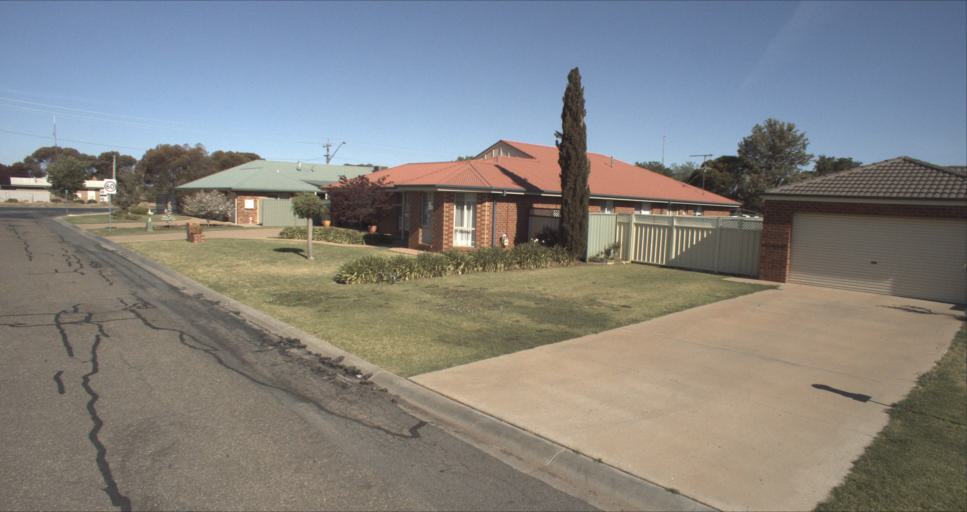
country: AU
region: New South Wales
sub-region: Leeton
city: Leeton
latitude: -34.5537
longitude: 146.4159
